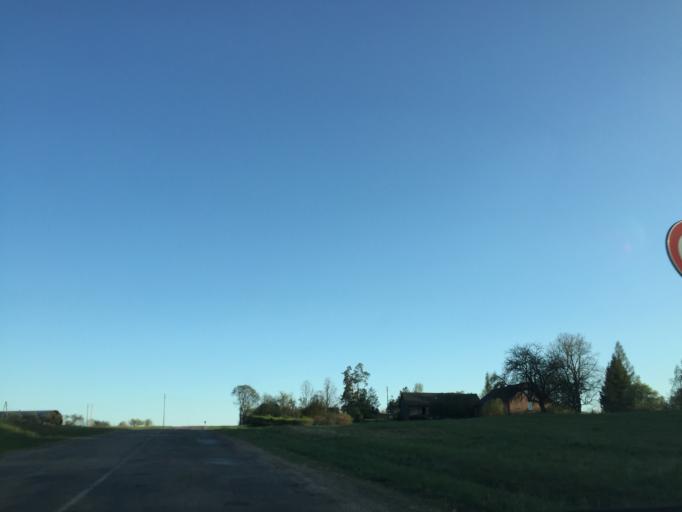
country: LV
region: Koknese
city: Koknese
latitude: 56.7119
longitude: 25.4933
